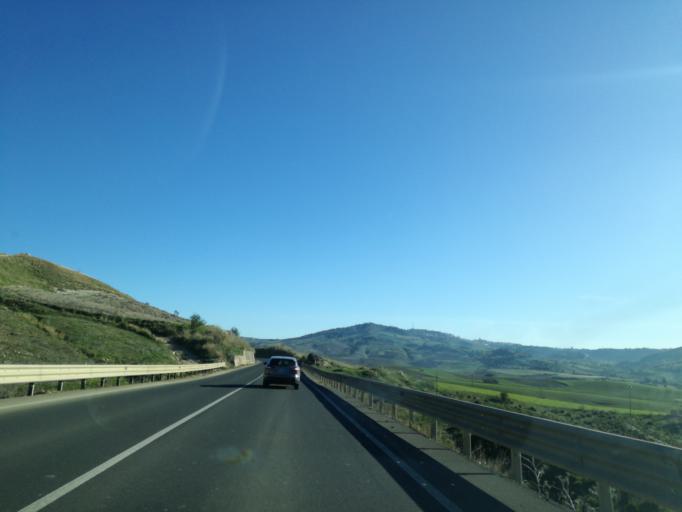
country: IT
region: Sicily
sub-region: Catania
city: San Michele di Ganzaria
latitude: 37.2400
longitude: 14.4545
